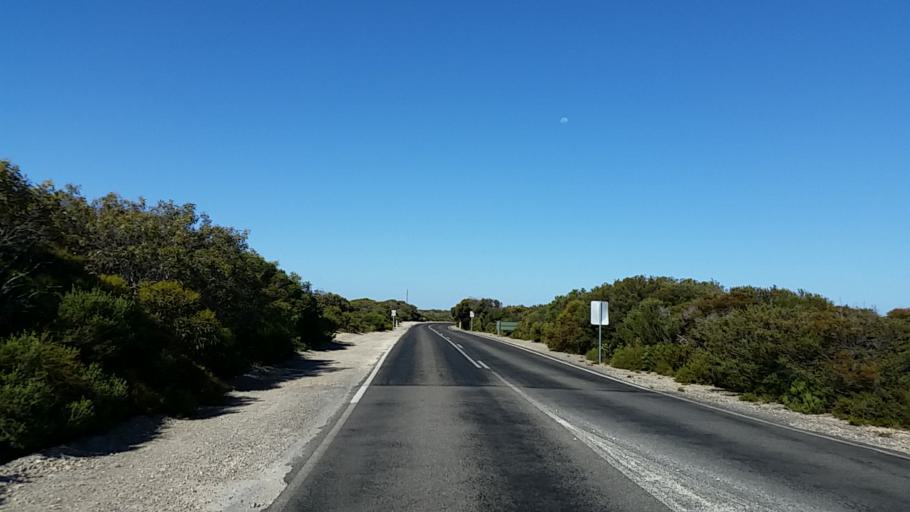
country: AU
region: South Australia
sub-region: Yorke Peninsula
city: Honiton
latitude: -35.2677
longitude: 136.9417
